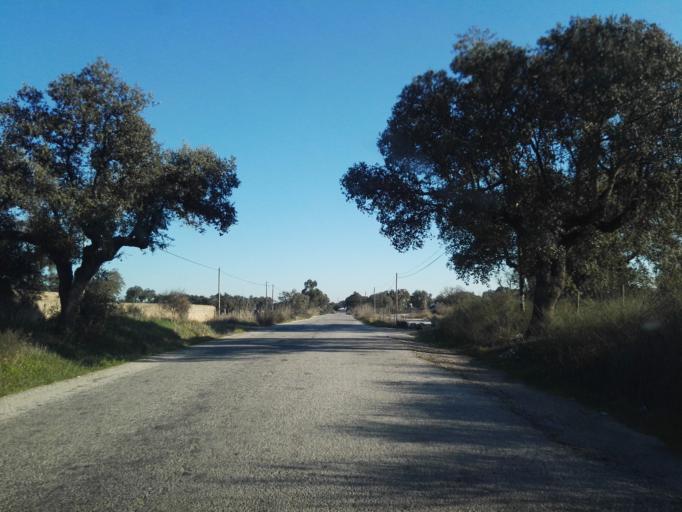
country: PT
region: Evora
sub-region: Evora
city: Evora
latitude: 38.5390
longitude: -7.9552
